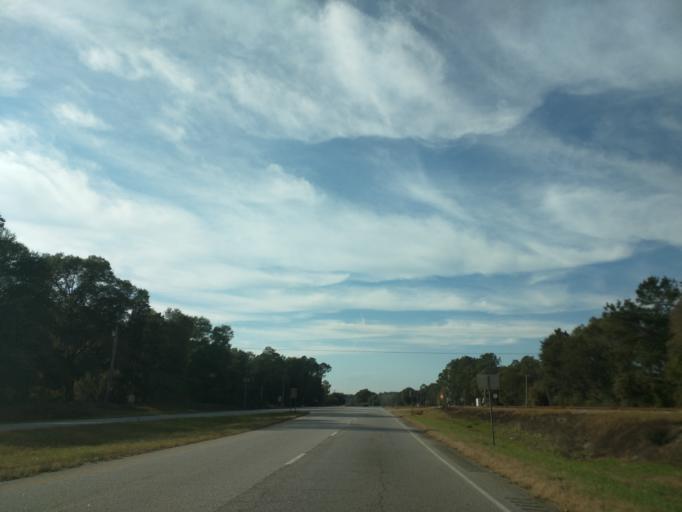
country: US
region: Georgia
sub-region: Decatur County
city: Bainbridge
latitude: 30.9005
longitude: -84.5223
